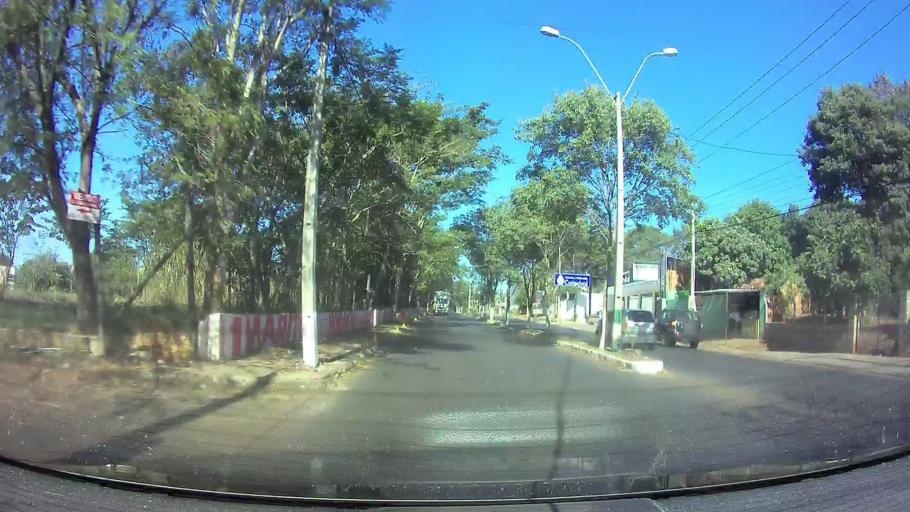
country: PY
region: Central
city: Villa Elisa
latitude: -25.3688
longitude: -57.5785
